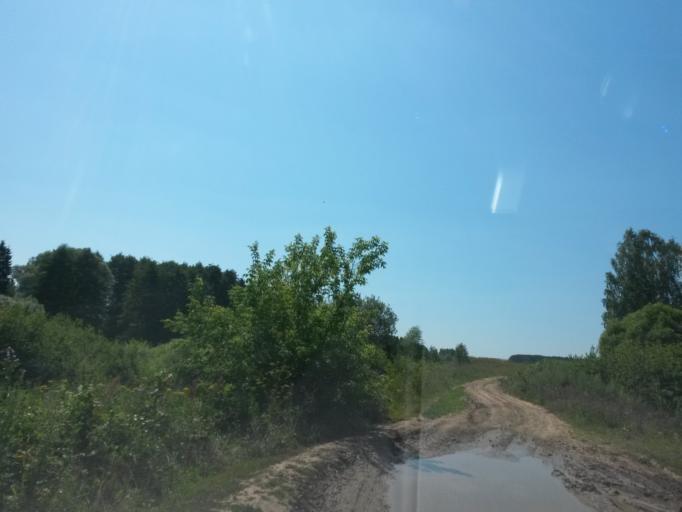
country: RU
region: Moskovskaya
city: Stolbovaya
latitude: 55.2690
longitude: 37.4838
